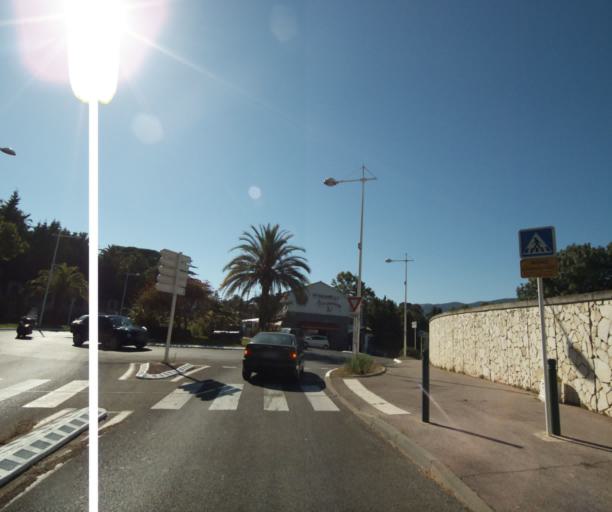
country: FR
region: Provence-Alpes-Cote d'Azur
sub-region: Departement du Var
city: La Valette-du-Var
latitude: 43.1095
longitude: 5.9808
